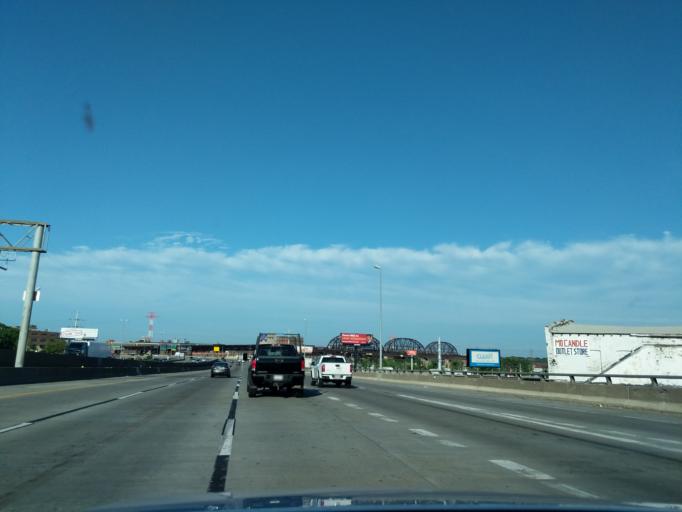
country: US
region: Missouri
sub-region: City of Saint Louis
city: St. Louis
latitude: 38.6134
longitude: -90.1968
